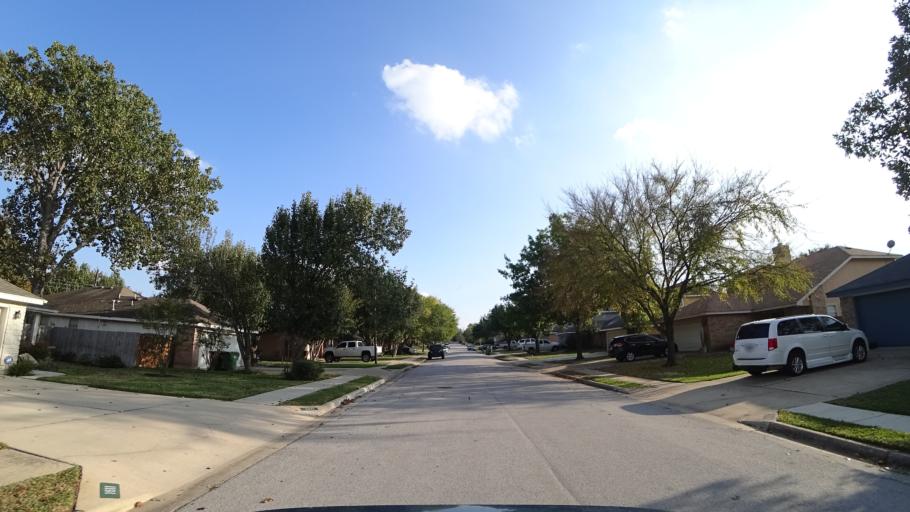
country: US
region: Texas
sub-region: Williamson County
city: Round Rock
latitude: 30.4943
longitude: -97.6637
